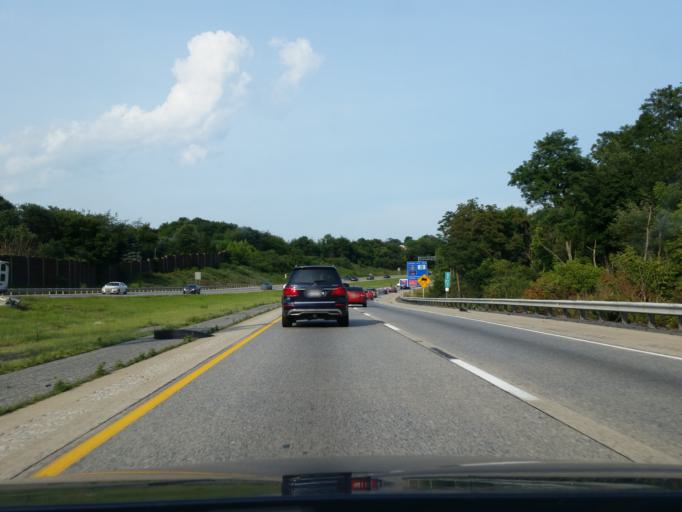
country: US
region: Pennsylvania
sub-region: Dauphin County
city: Paxtonia
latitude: 40.3248
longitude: -76.8092
